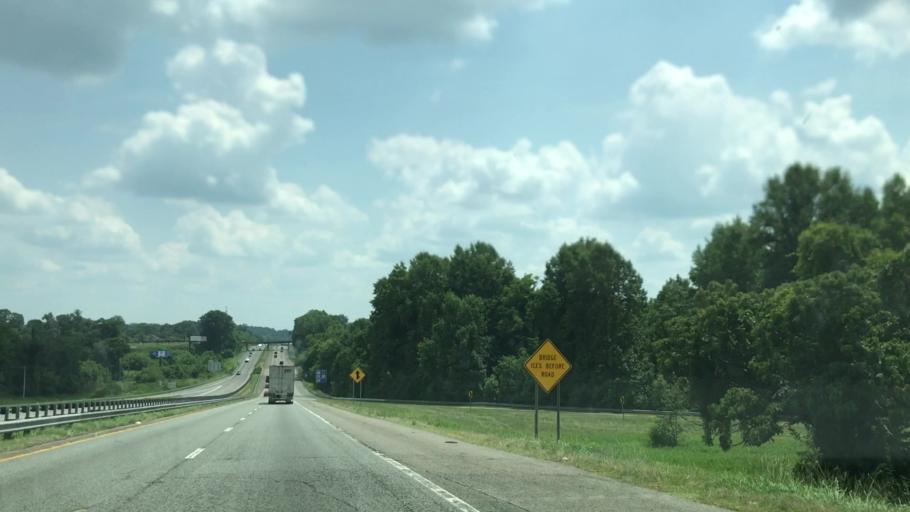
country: US
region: North Carolina
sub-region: Iredell County
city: Statesville
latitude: 35.8082
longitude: -80.8613
